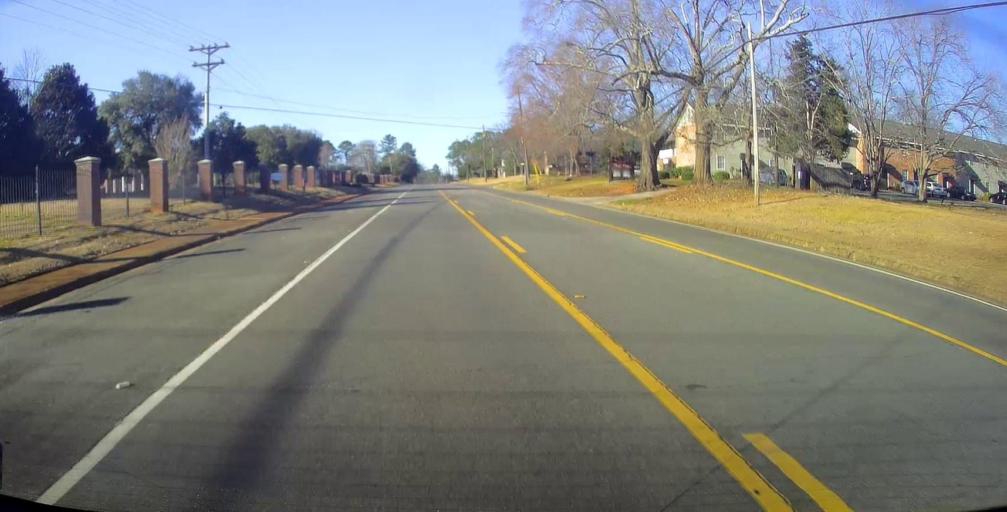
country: US
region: Georgia
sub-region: Sumter County
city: Americus
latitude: 32.0450
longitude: -84.2230
